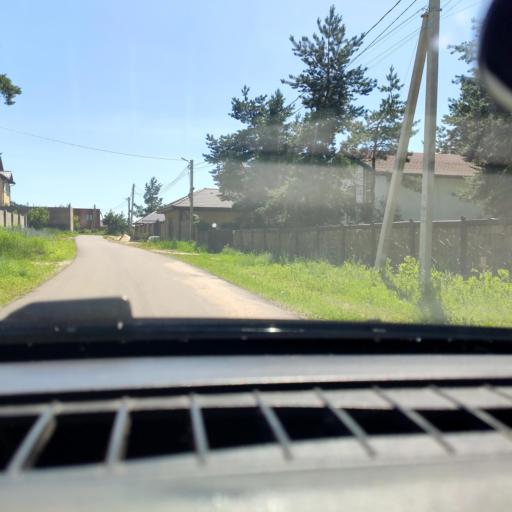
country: RU
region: Voronezj
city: Podgornoye
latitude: 51.7946
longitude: 39.1355
